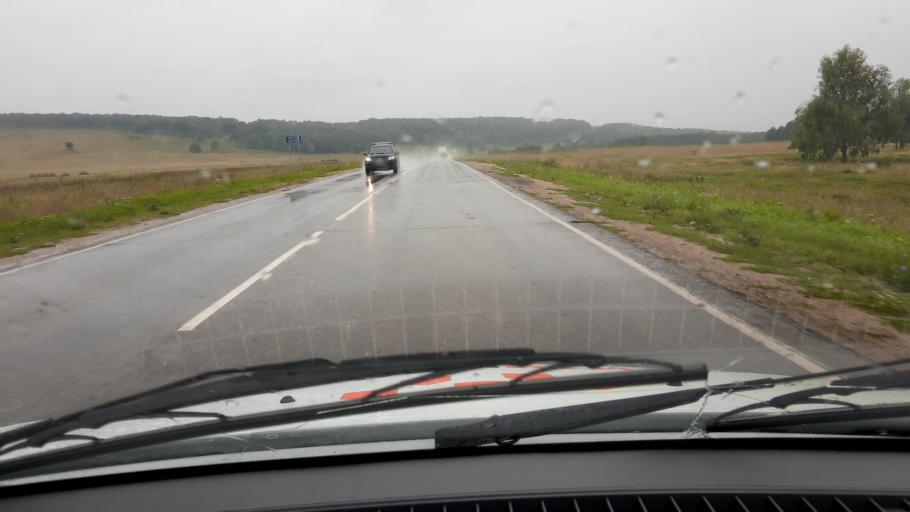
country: RU
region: Bashkortostan
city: Iglino
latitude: 54.9462
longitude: 56.4807
